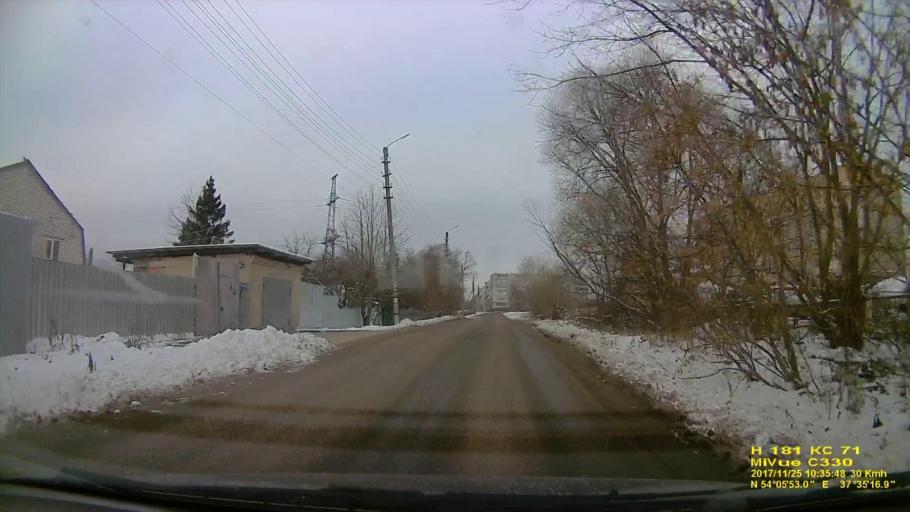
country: RU
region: Tula
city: Skuratovskiy
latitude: 54.0981
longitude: 37.5876
